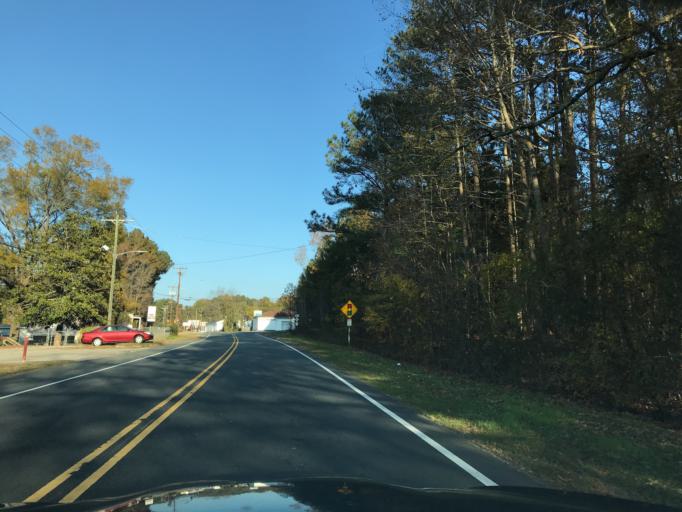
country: US
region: North Carolina
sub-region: Granville County
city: Creedmoor
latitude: 36.1208
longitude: -78.6924
